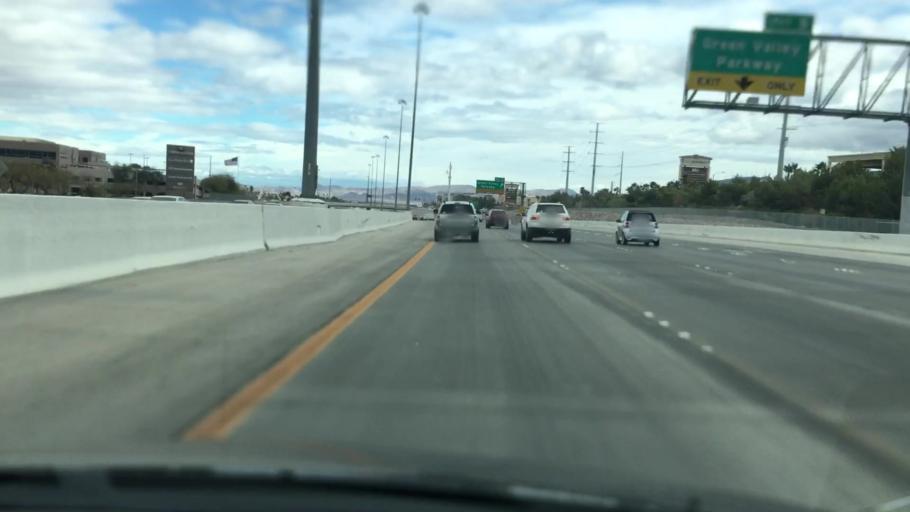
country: US
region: Nevada
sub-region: Clark County
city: Whitney
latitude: 36.0234
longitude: -115.0916
